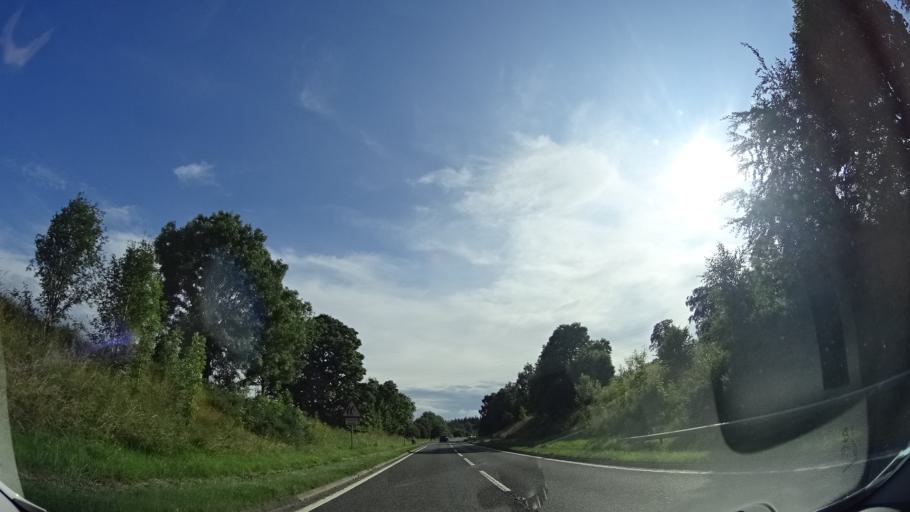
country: GB
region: Scotland
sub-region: Highland
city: Conon Bridge
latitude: 57.5768
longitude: -4.4478
